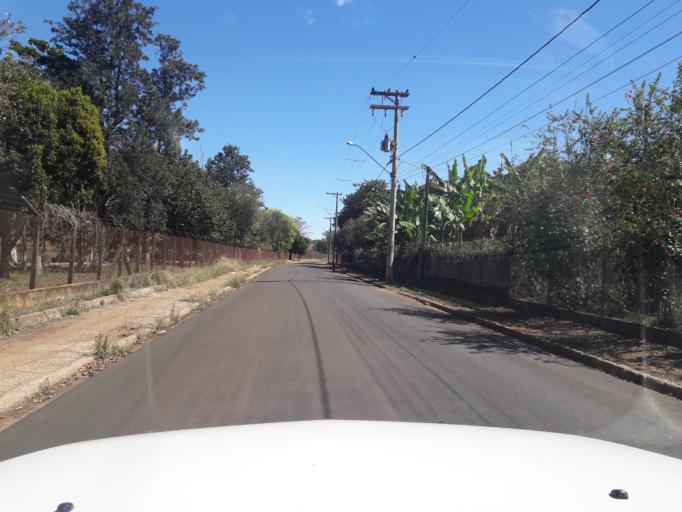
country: BR
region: Sao Paulo
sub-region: Moji-Guacu
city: Mogi-Gaucu
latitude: -22.3413
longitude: -46.9323
